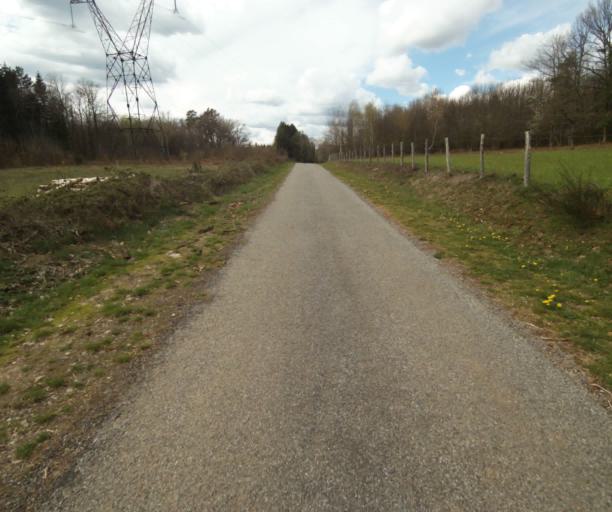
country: FR
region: Limousin
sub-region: Departement de la Correze
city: Argentat
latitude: 45.1871
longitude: 1.9156
